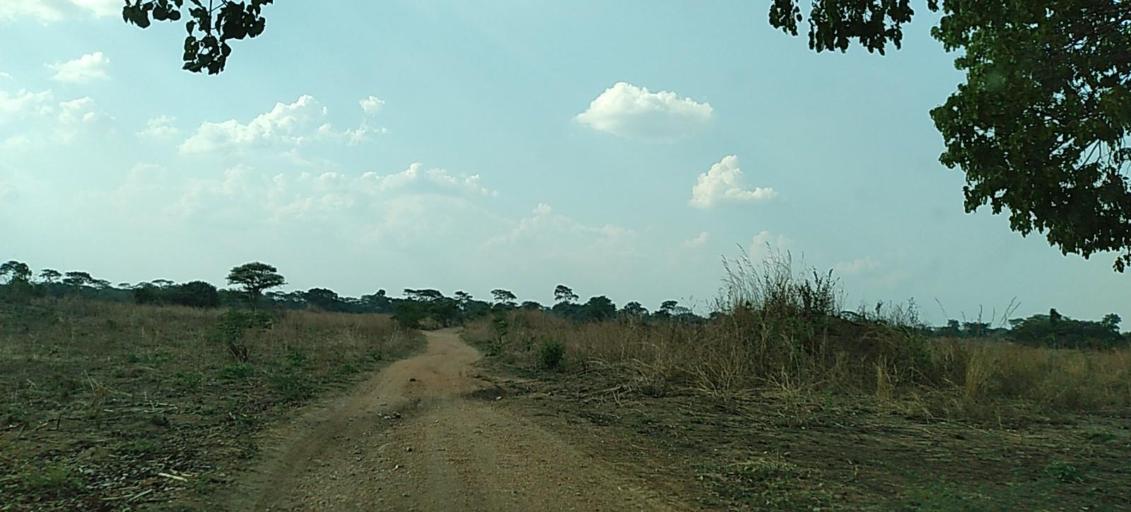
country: ZM
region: Copperbelt
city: Mpongwe
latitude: -13.5016
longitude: 28.0887
